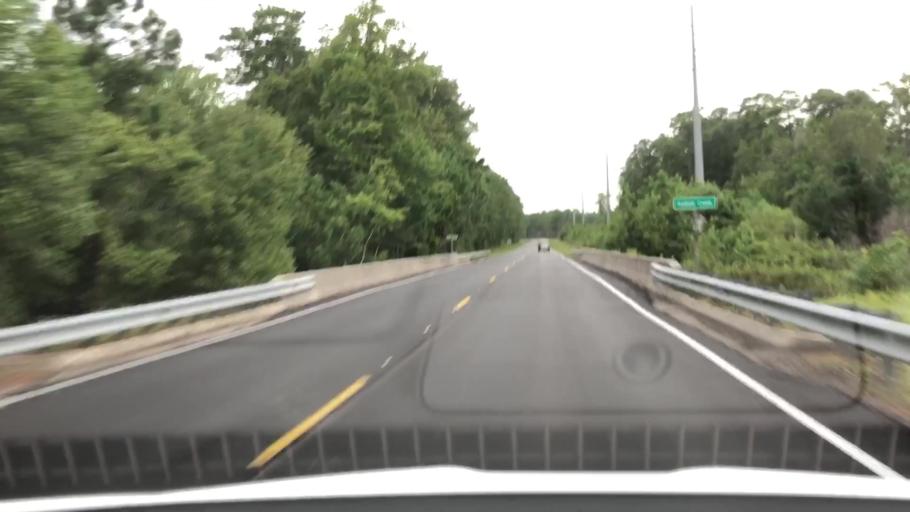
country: US
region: North Carolina
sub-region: Carteret County
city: Cape Carteret
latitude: 34.7661
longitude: -77.0962
